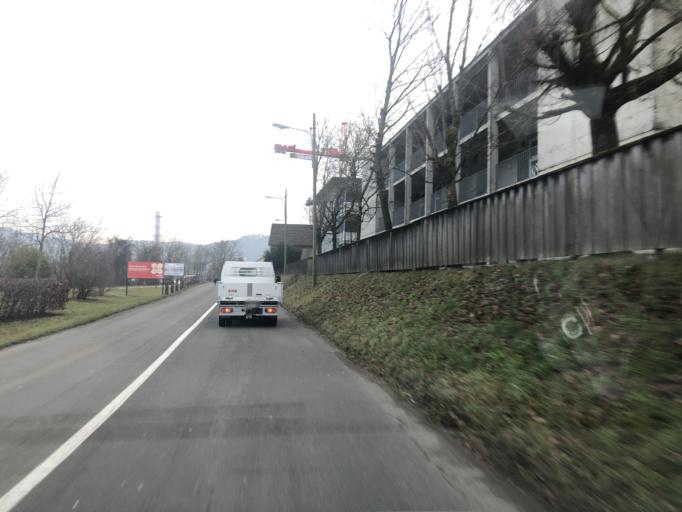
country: CH
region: Aargau
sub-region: Bezirk Baden
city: Turgi
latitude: 47.4877
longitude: 8.2629
